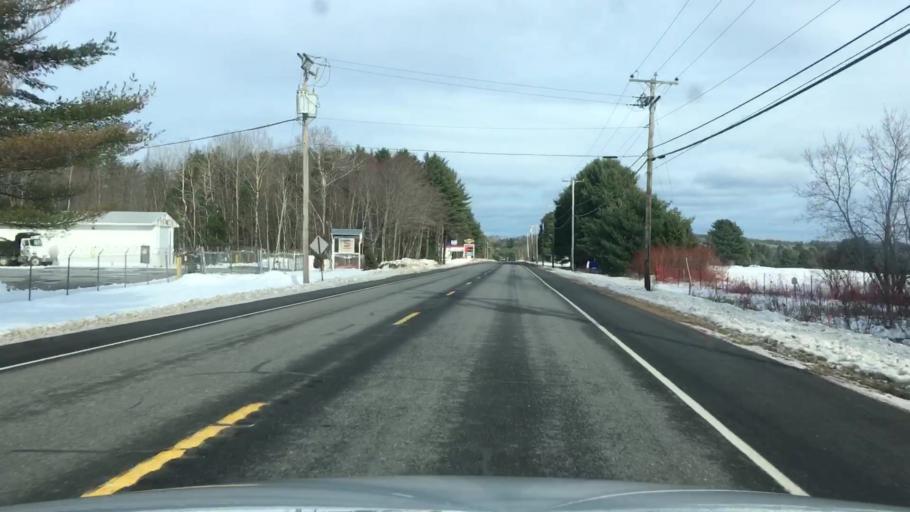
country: US
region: Maine
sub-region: Androscoggin County
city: Greene
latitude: 44.2206
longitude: -70.0911
